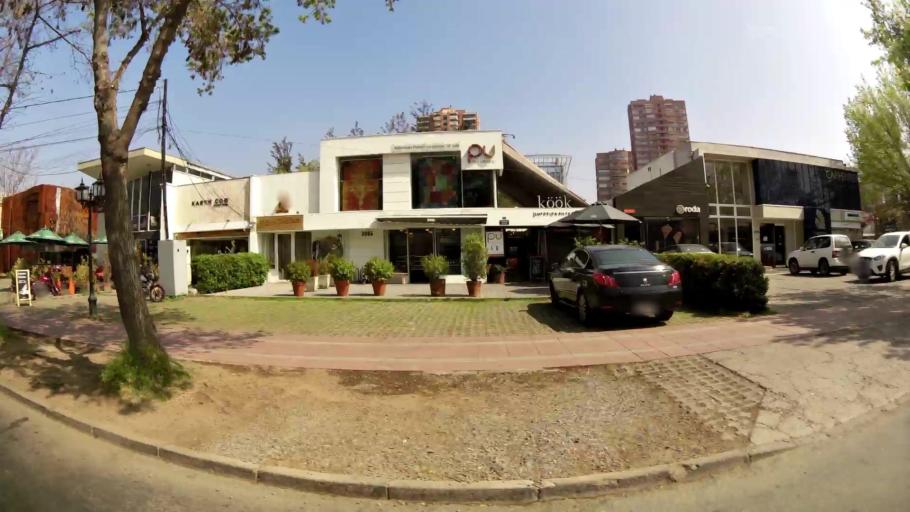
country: CL
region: Santiago Metropolitan
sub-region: Provincia de Santiago
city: Villa Presidente Frei, Nunoa, Santiago, Chile
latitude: -33.3972
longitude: -70.5977
